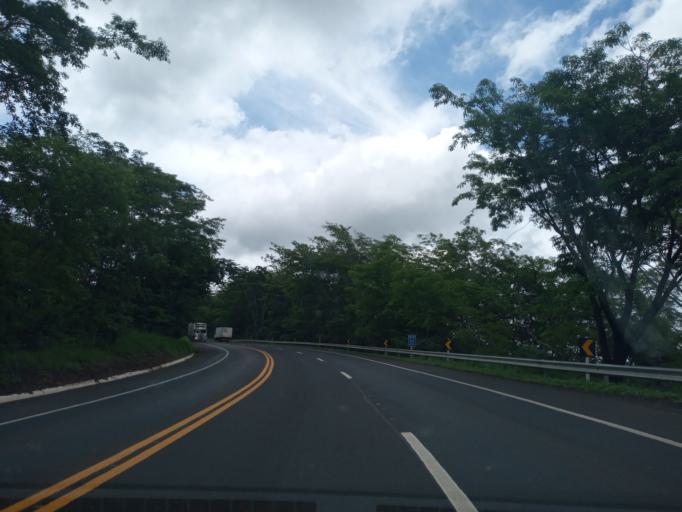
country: BR
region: Minas Gerais
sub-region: Monte Carmelo
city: Monte Carmelo
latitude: -19.2616
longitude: -47.6464
